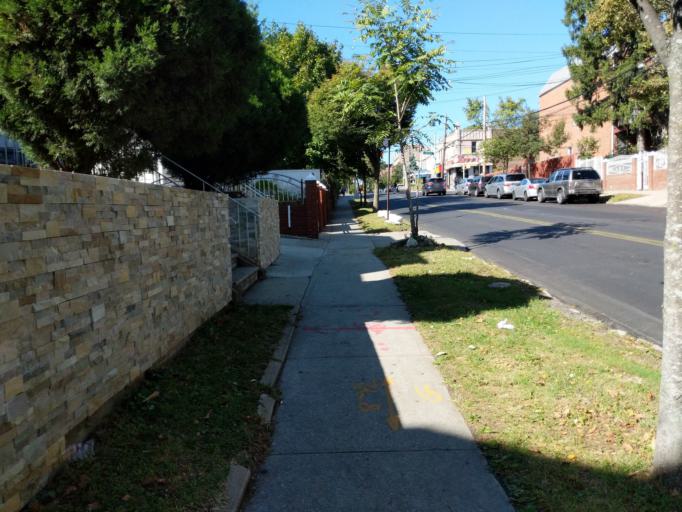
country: US
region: New York
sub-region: Queens County
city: Jamaica
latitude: 40.7120
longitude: -73.8010
